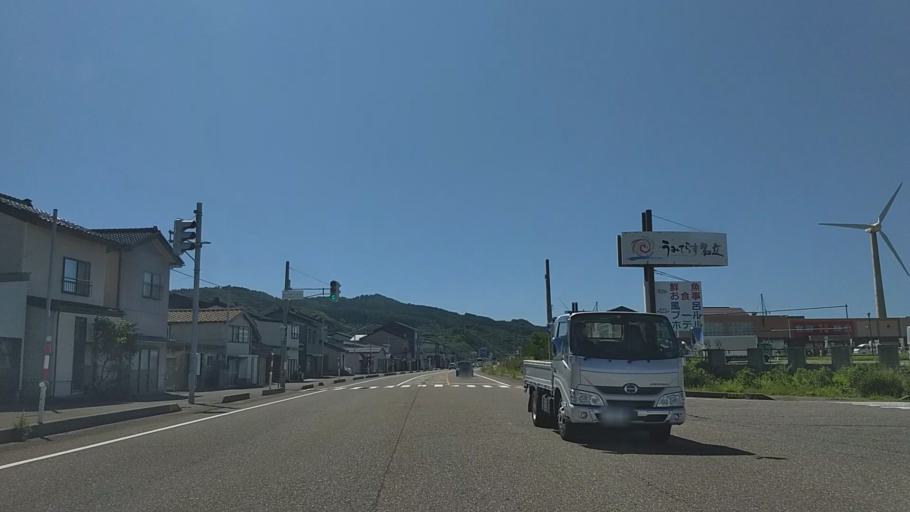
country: JP
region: Niigata
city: Joetsu
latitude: 37.1646
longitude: 138.0885
